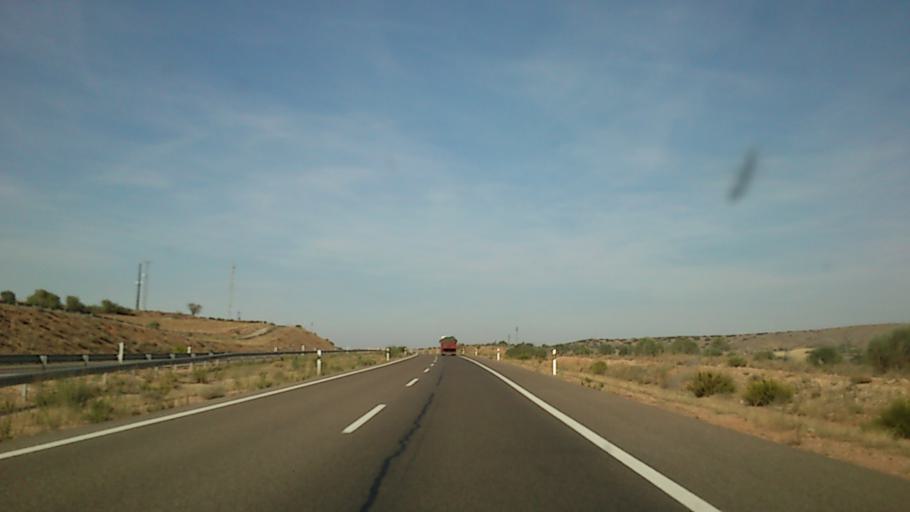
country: ES
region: Aragon
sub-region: Provincia de Zaragoza
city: Longares
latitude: 41.4165
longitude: -1.1602
